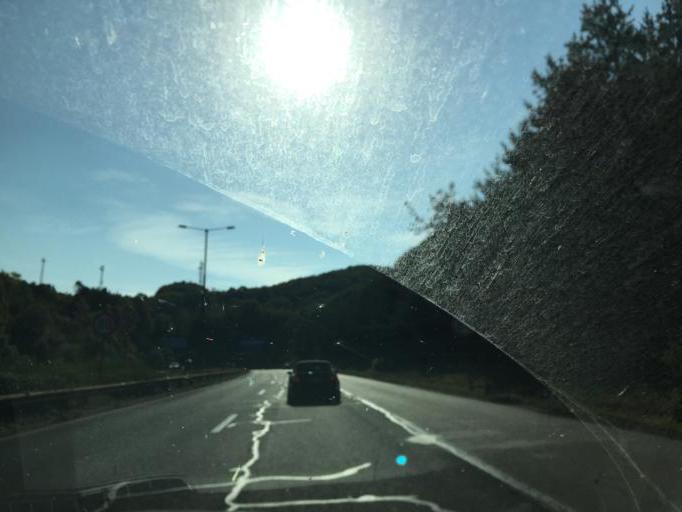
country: BG
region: Sofiya
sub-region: Obshtina Ikhtiman
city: Ikhtiman
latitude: 42.3566
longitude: 23.9110
